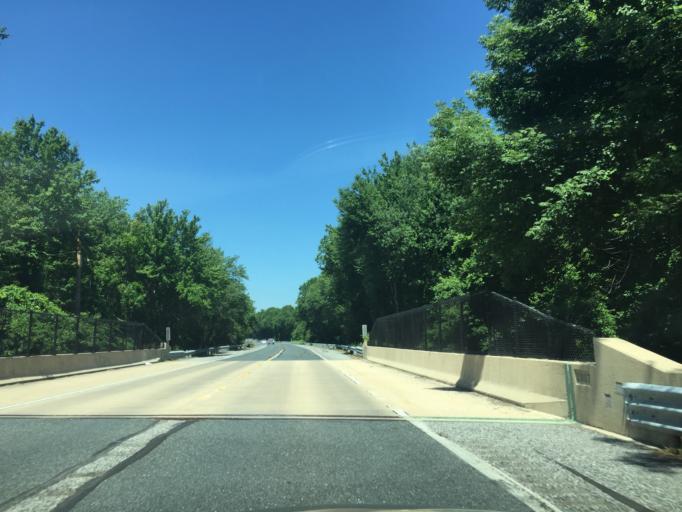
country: US
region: Maryland
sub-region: Harford County
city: Jarrettsville
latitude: 39.5834
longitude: -76.4539
